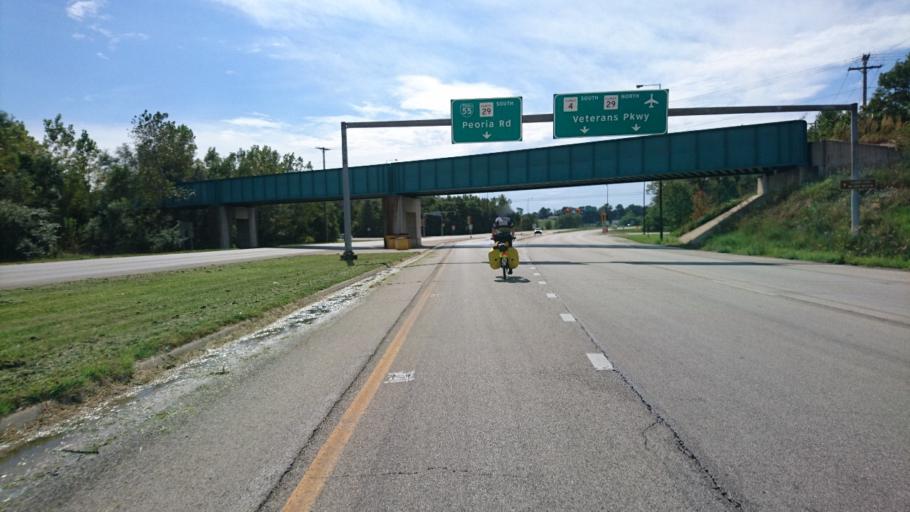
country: US
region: Illinois
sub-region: Sangamon County
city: Grandview
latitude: 39.8465
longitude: -89.6313
